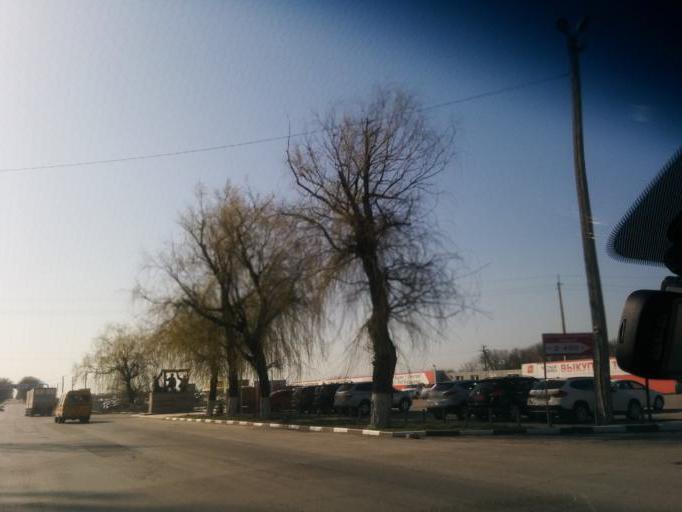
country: RU
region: Rostov
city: Mayskiy
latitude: 47.7121
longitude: 40.1380
